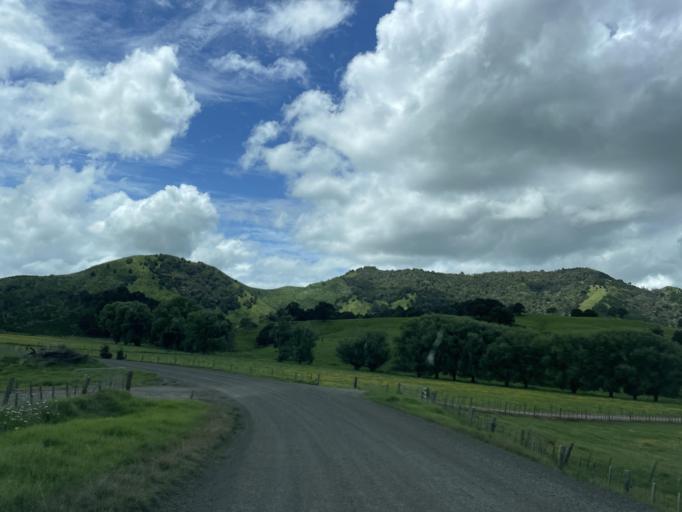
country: NZ
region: Northland
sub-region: Kaipara District
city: Dargaville
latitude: -35.8665
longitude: 174.0353
